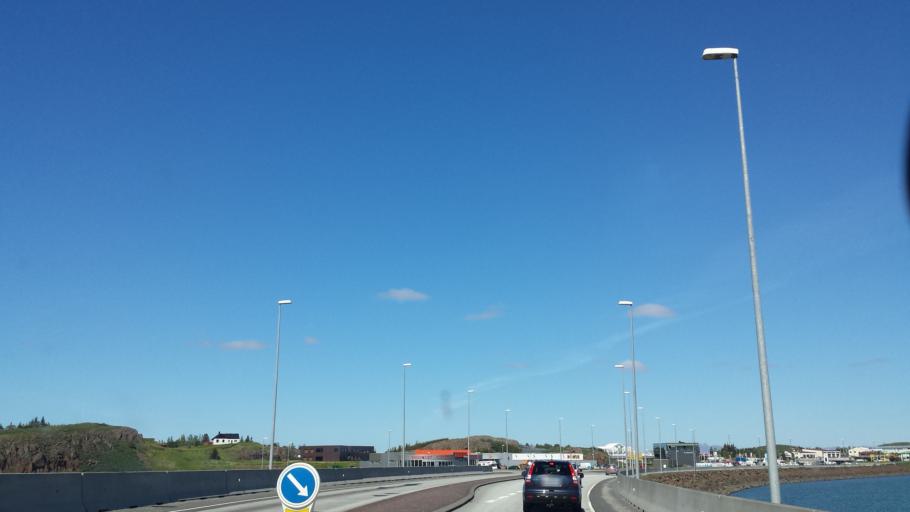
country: IS
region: West
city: Borgarnes
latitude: 64.5390
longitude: -21.9054
